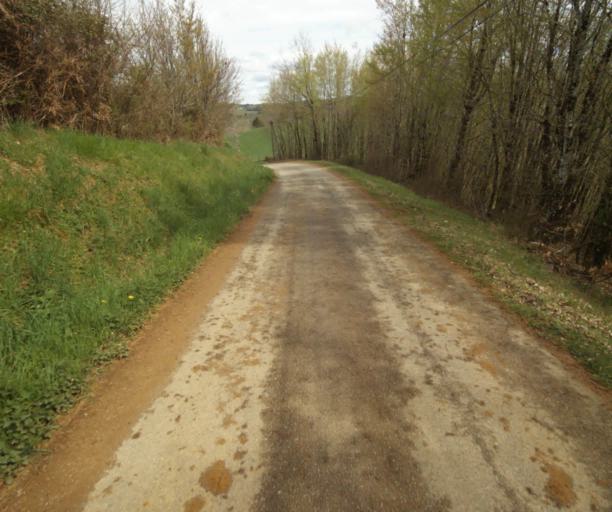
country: FR
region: Limousin
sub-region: Departement de la Correze
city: Laguenne
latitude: 45.2286
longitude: 1.8493
